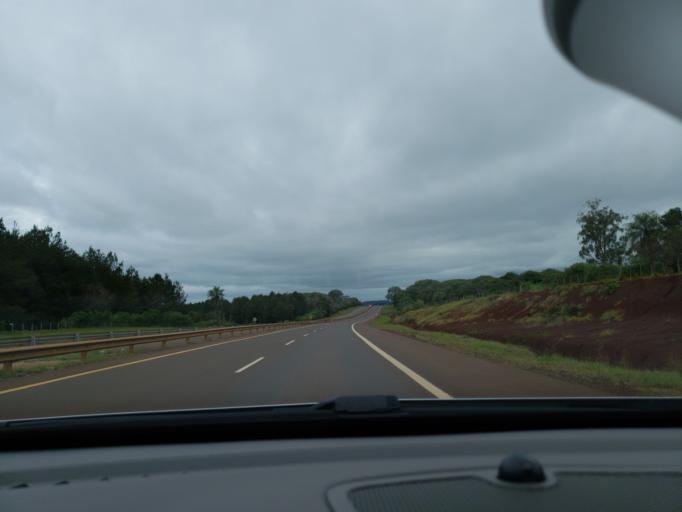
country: AR
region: Misiones
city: Garupa
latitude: -27.5391
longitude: -55.8539
